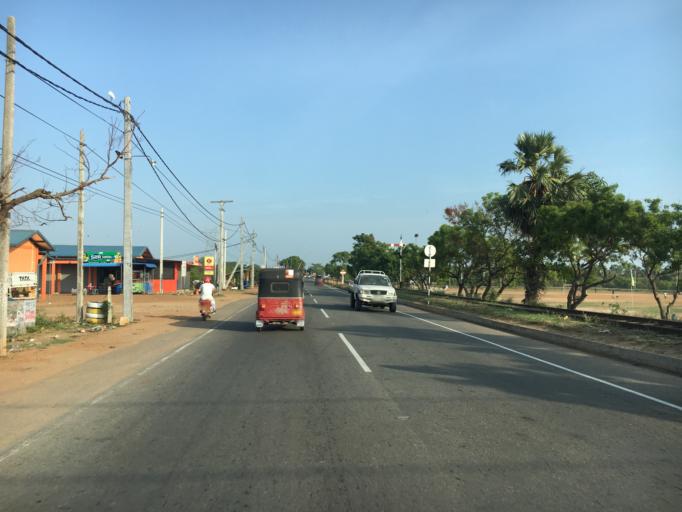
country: LK
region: Eastern Province
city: Eravur Town
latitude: 7.9180
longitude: 81.5187
